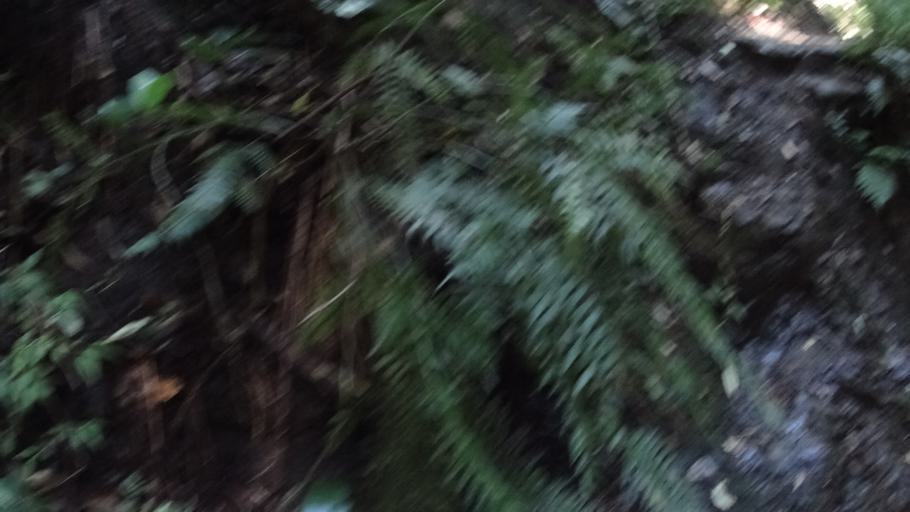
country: JP
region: Kanagawa
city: Hayama
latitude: 35.2815
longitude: 139.6083
